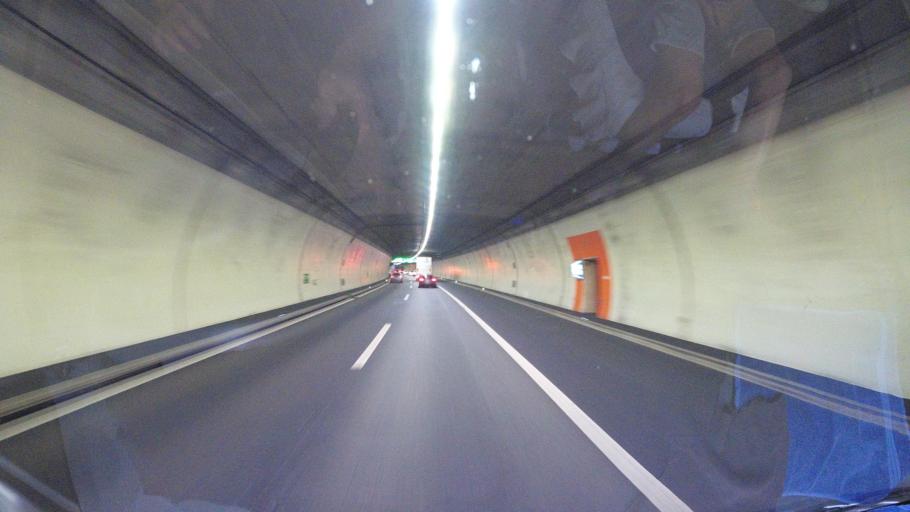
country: CH
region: Zurich
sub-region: Bezirk Dietikon
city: Birmensdorf
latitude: 47.3437
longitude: 8.4449
